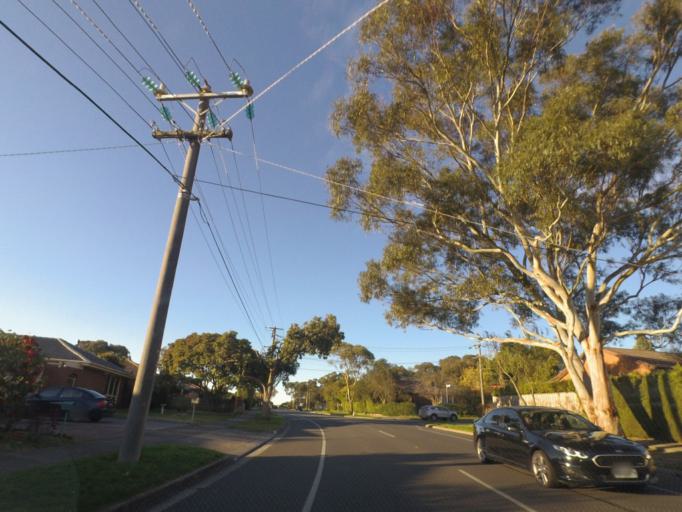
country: AU
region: Victoria
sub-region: Maroondah
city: Warranwood
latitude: -37.7870
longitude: 145.2392
